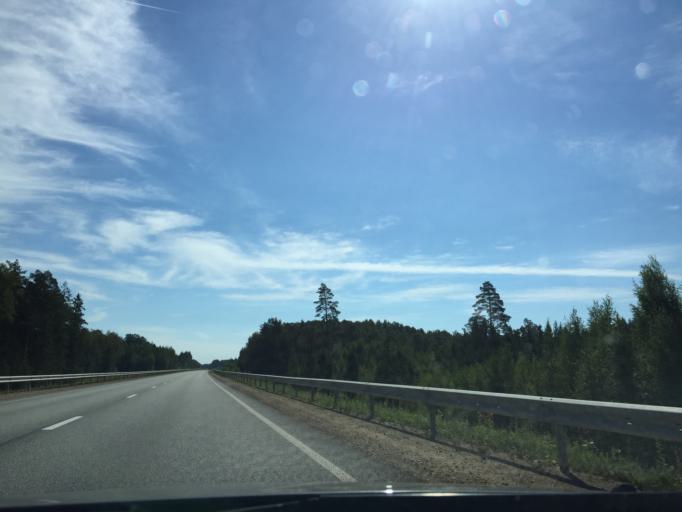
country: LV
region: Skriveri
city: Skriveri
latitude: 56.7198
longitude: 25.1975
